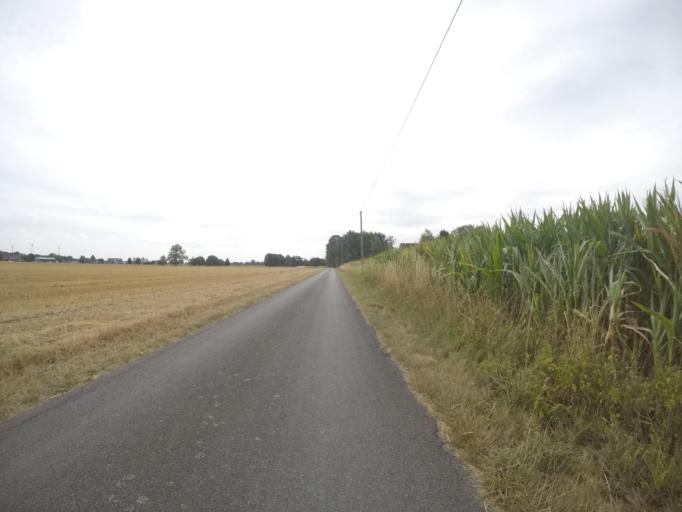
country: NL
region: Gelderland
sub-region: Gemeente Aalten
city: Aalten
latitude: 51.8610
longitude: 6.5453
